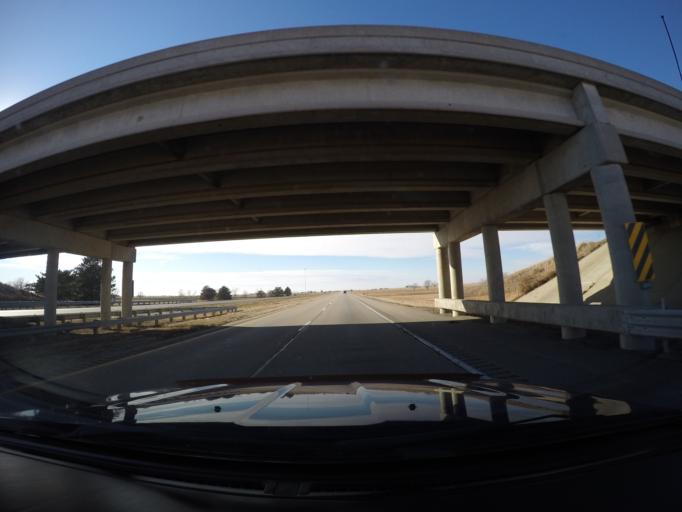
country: US
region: Nebraska
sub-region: Hamilton County
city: Aurora
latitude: 40.8213
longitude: -97.8072
